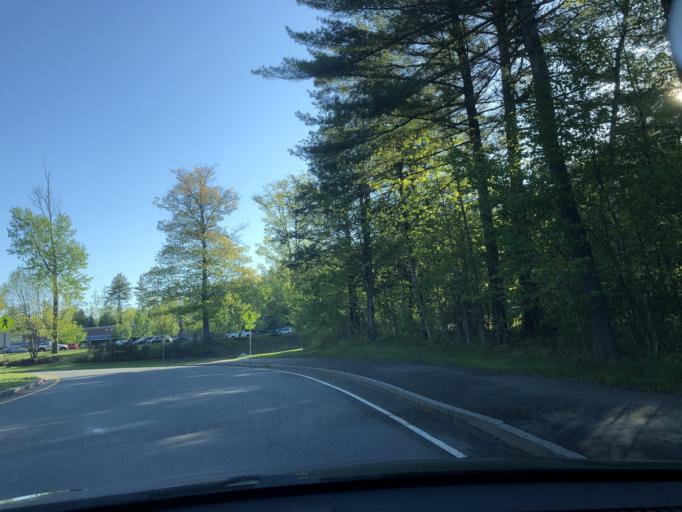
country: US
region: New Hampshire
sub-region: Grafton County
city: Lebanon
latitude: 43.6745
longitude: -72.2607
